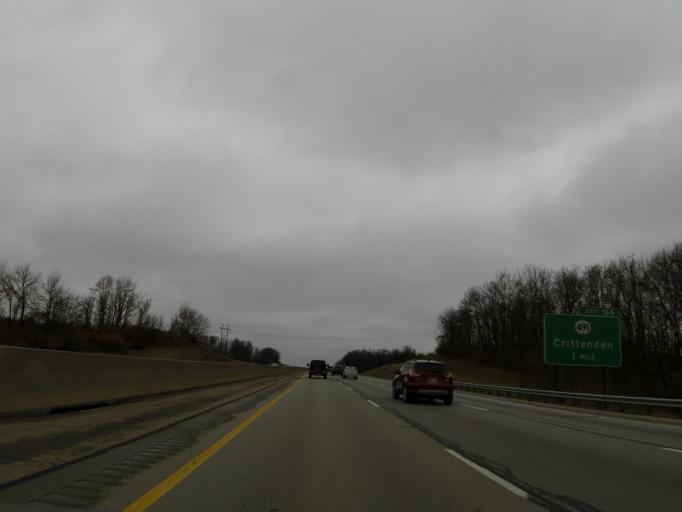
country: US
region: Kentucky
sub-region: Grant County
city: Crittenden
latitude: 38.8080
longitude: -84.6023
